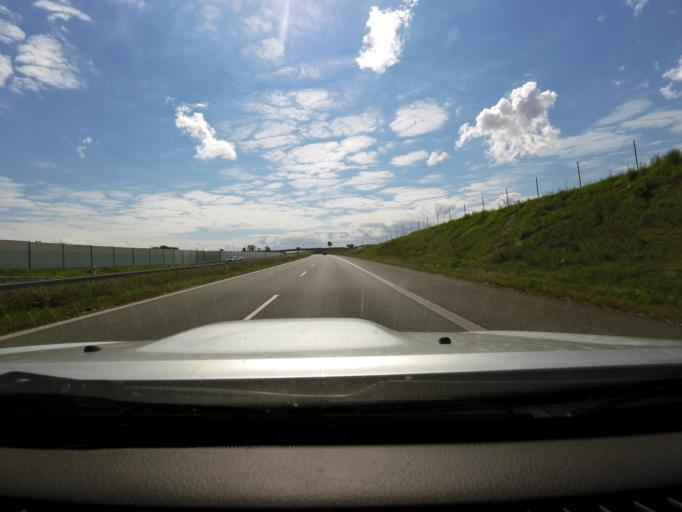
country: PL
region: Warmian-Masurian Voivodeship
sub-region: Powiat ostrodzki
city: Maldyty
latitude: 53.8483
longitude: 19.7517
